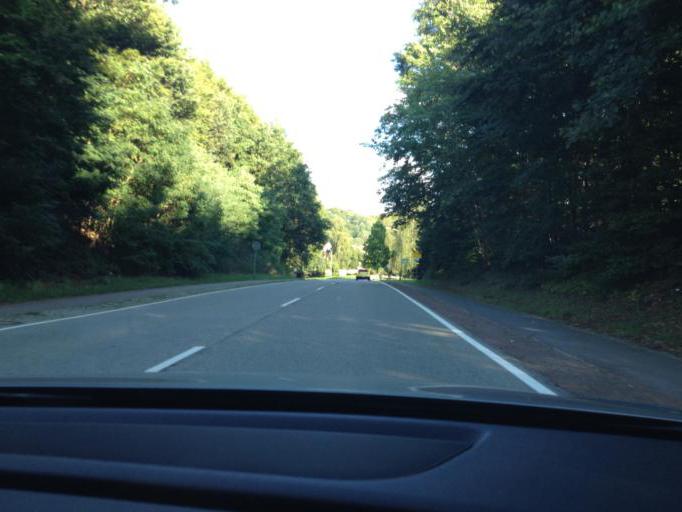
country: DE
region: Saarland
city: Tholey
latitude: 49.5032
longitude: 7.0152
